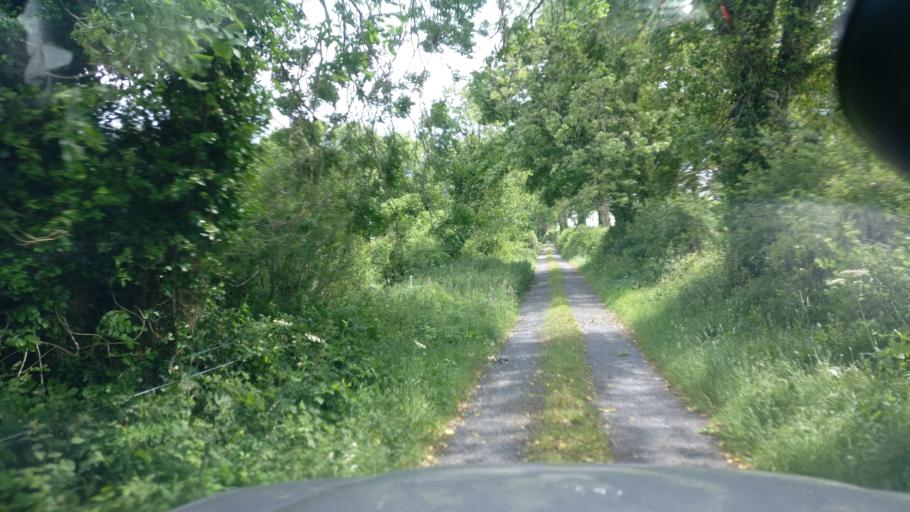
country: IE
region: Connaught
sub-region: County Galway
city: Ballinasloe
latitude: 53.2714
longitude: -8.3332
